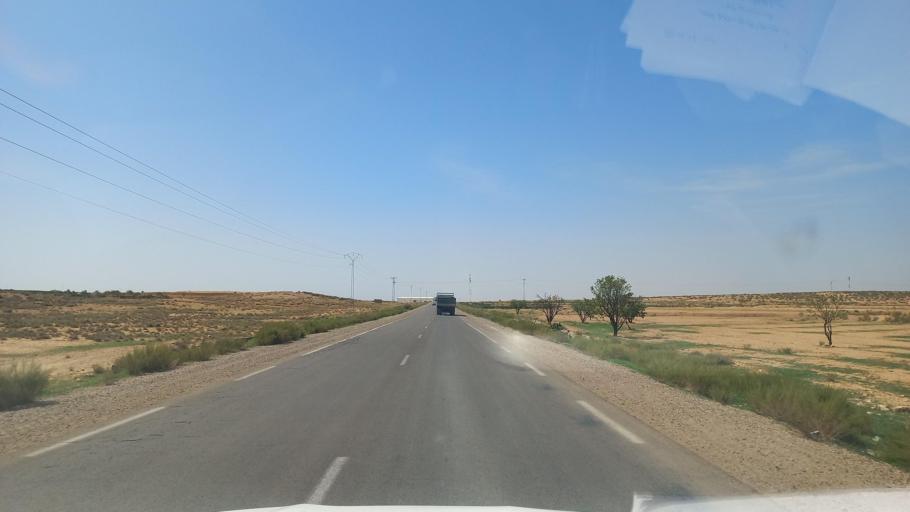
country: TN
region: Al Qasrayn
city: Sbiba
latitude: 35.3829
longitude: 9.1107
